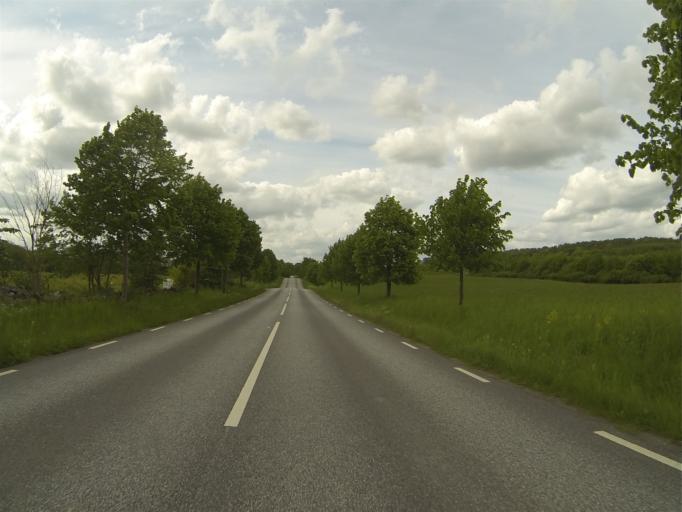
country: SE
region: Skane
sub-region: Sjobo Kommun
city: Sjoebo
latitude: 55.6702
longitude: 13.6658
